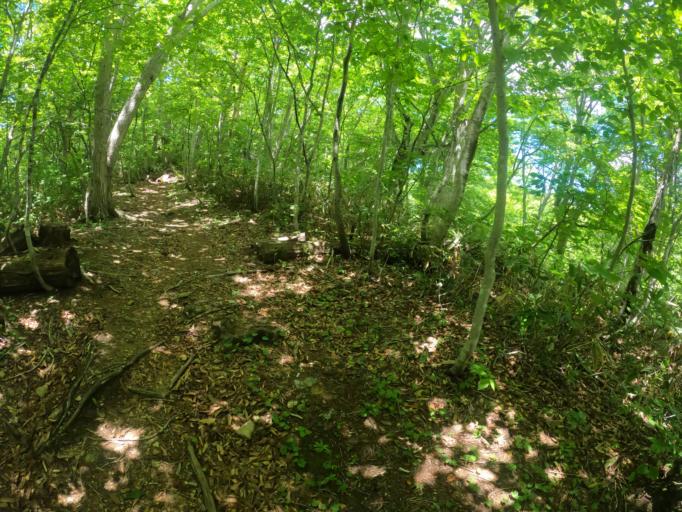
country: JP
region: Iwate
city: Ichinoseki
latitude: 38.9232
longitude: 140.7971
